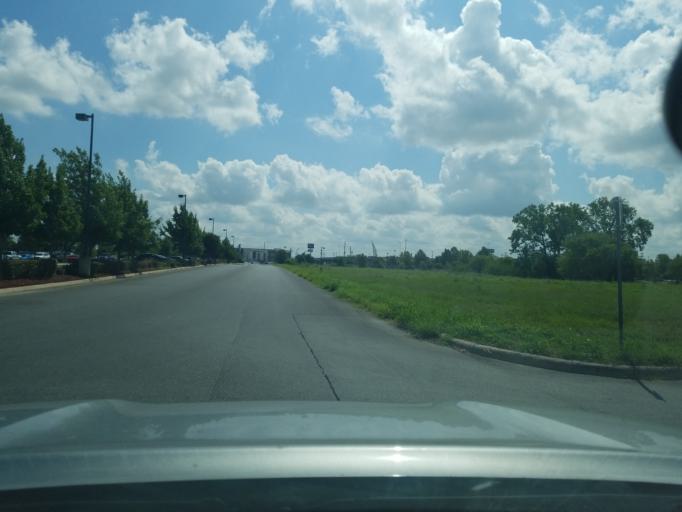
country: US
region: Texas
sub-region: Bexar County
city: San Antonio
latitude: 29.3521
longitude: -98.5380
